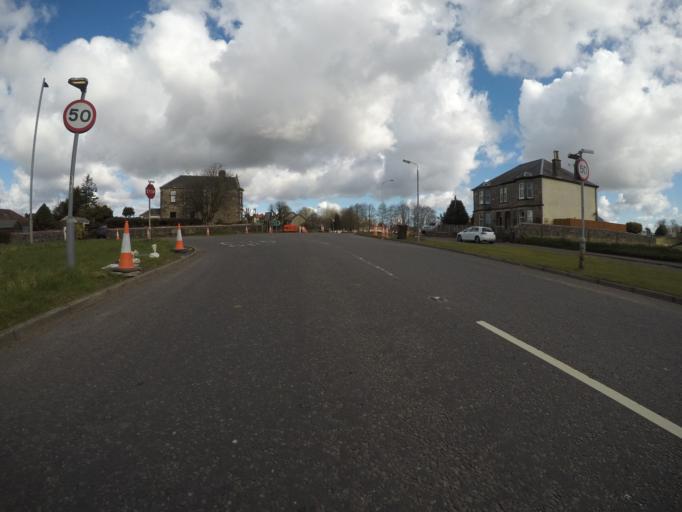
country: GB
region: Scotland
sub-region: North Ayrshire
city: Beith
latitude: 55.7461
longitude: -4.6293
